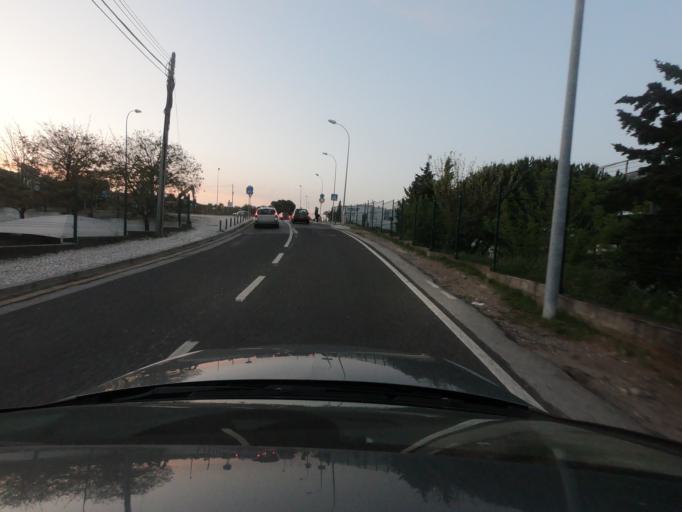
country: PT
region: Lisbon
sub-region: Amadora
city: Amadora
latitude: 38.7368
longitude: -9.2314
